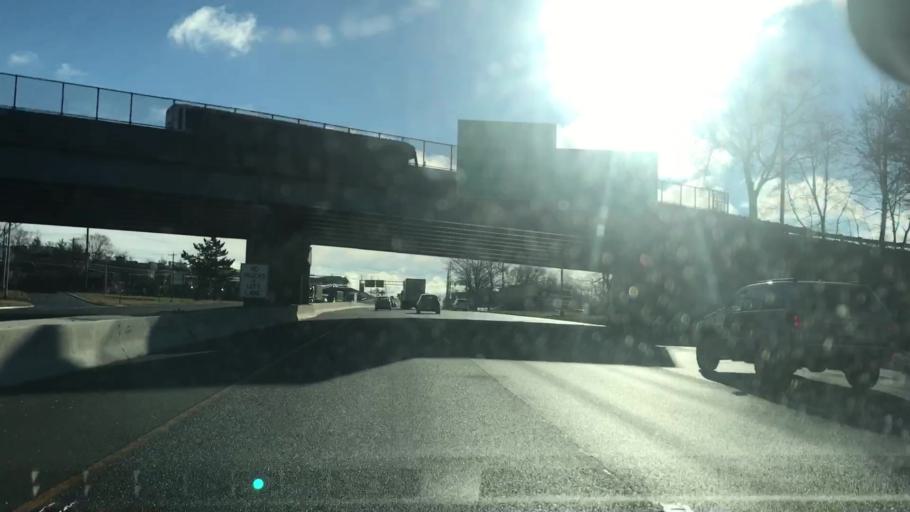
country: US
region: New Jersey
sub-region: Bergen County
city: Ramsey
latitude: 41.0697
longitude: -74.1372
